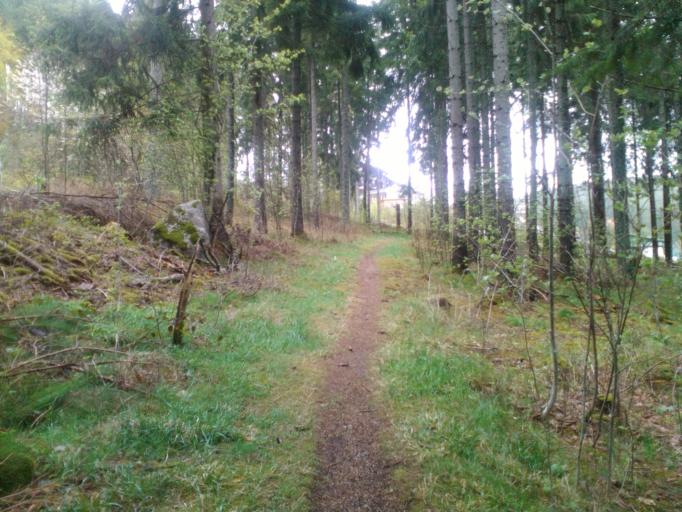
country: DE
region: Baden-Wuerttemberg
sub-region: Freiburg Region
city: Schluchsee
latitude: 47.8233
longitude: 8.1785
